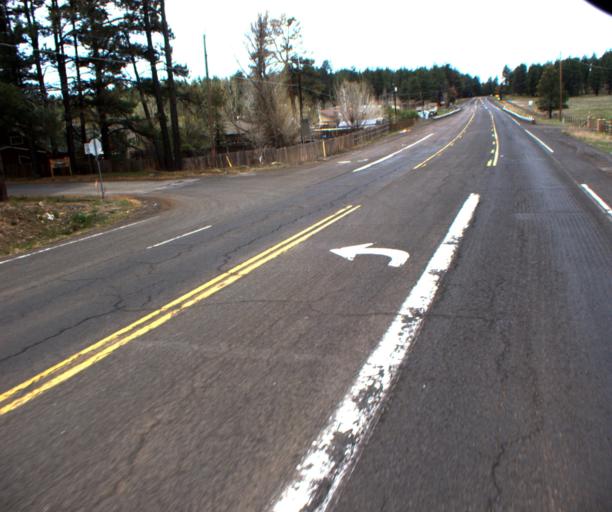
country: US
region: Arizona
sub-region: Coconino County
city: Kachina Village
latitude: 35.1301
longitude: -111.6900
